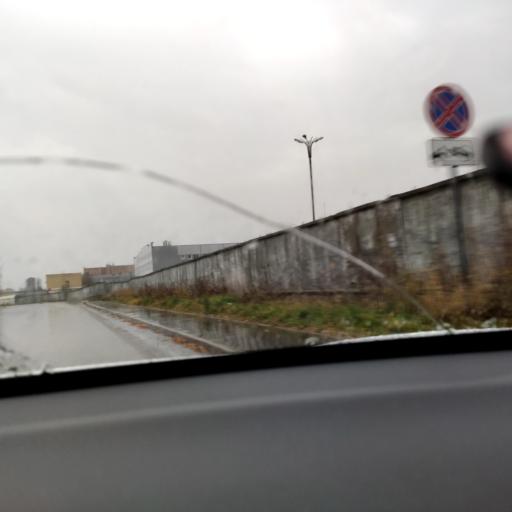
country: RU
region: Tatarstan
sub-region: Gorod Kazan'
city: Kazan
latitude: 55.8676
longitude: 49.1099
